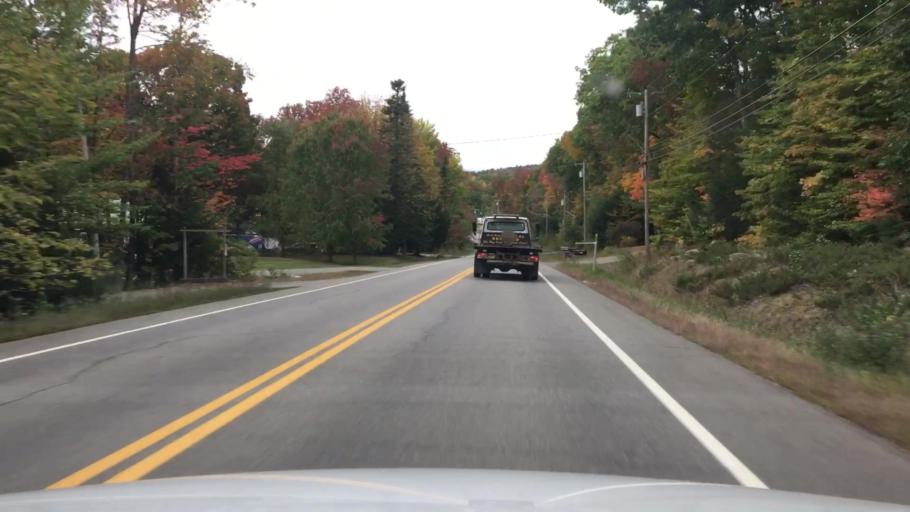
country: US
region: Maine
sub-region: Kennebec County
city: Oakland
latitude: 44.5606
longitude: -69.7445
